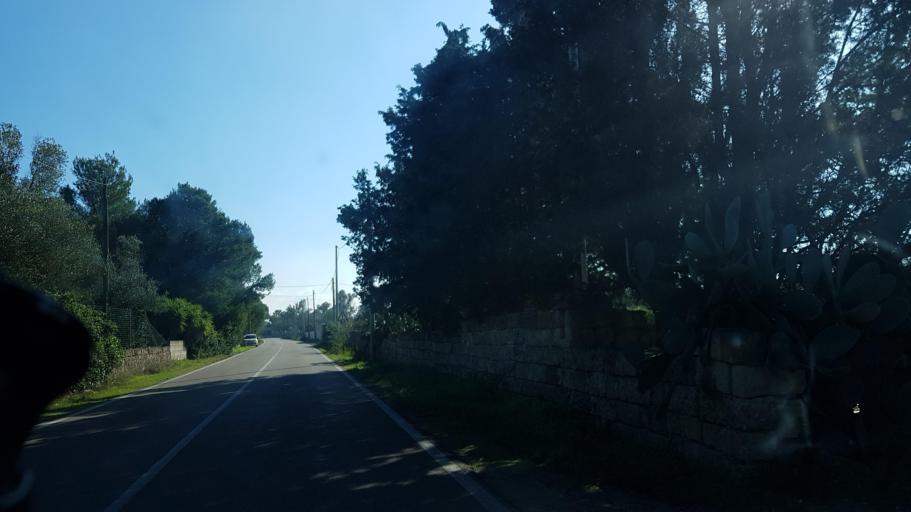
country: IT
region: Apulia
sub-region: Provincia di Lecce
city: Magliano
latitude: 40.3626
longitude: 18.0732
